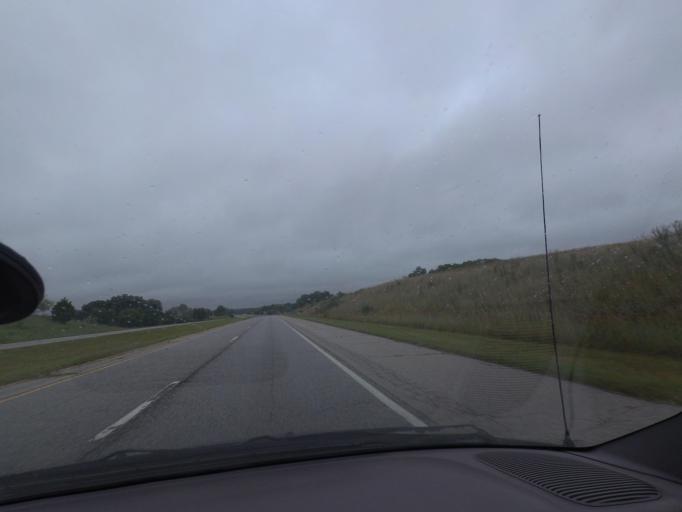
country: US
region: Illinois
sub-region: Pike County
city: Pittsfield
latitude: 39.6718
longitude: -90.7943
